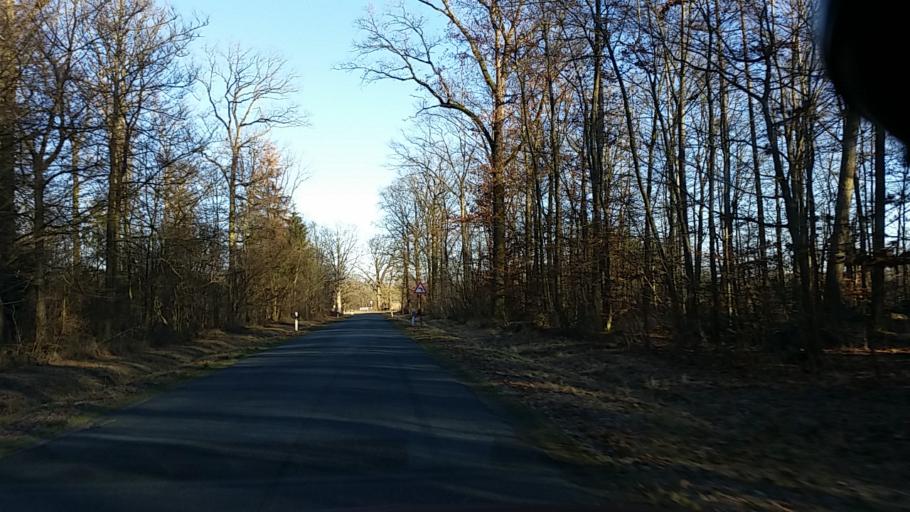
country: DE
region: Lower Saxony
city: Parsau
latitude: 52.5146
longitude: 10.9189
